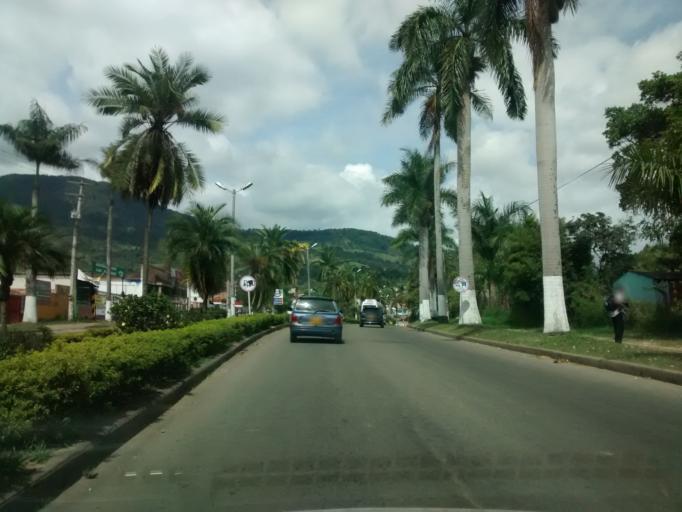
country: CO
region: Cundinamarca
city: Fusagasuga
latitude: 4.3423
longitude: -74.3693
